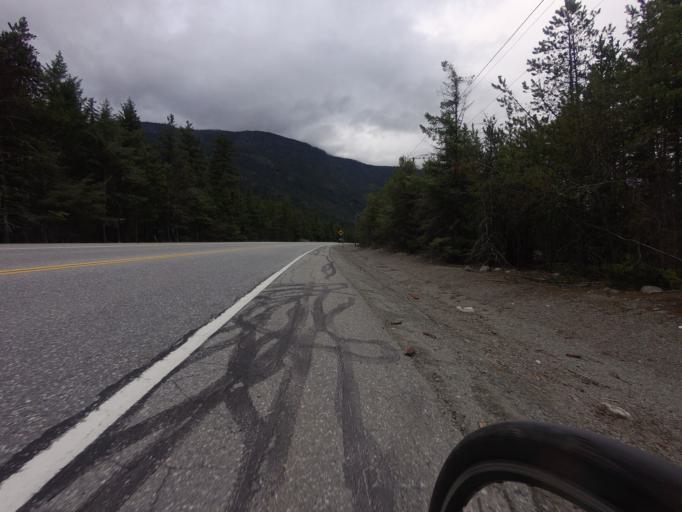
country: CA
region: British Columbia
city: Pemberton
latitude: 50.2661
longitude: -122.8674
